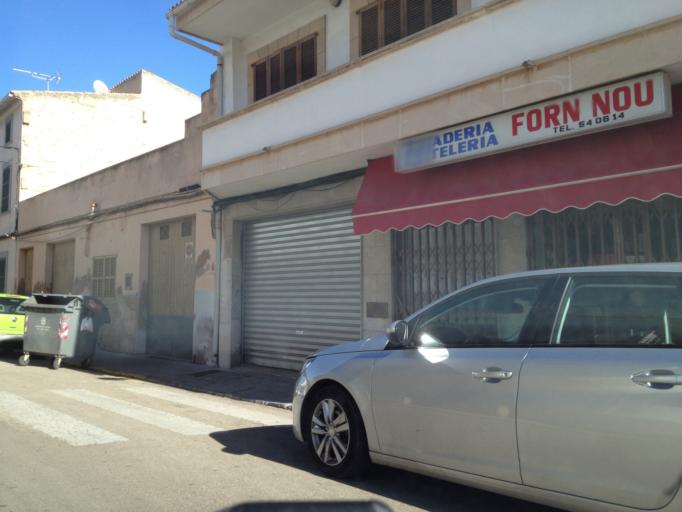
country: ES
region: Balearic Islands
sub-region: Illes Balears
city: sa Pobla
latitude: 39.7698
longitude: 3.0287
